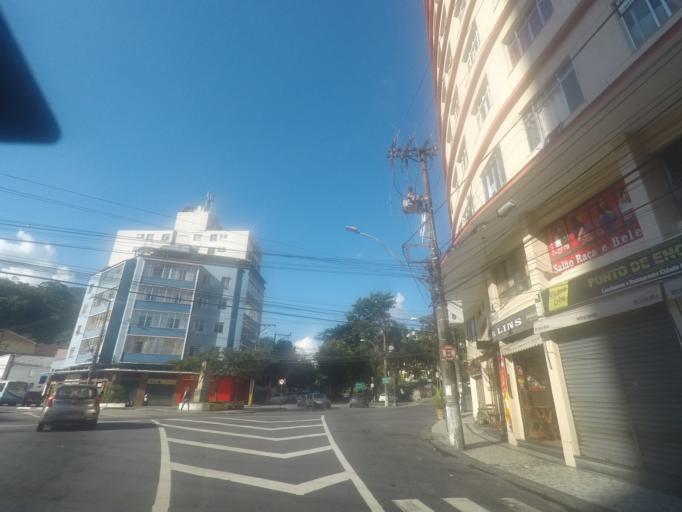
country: BR
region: Rio de Janeiro
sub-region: Petropolis
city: Petropolis
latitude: -22.5089
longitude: -43.1693
